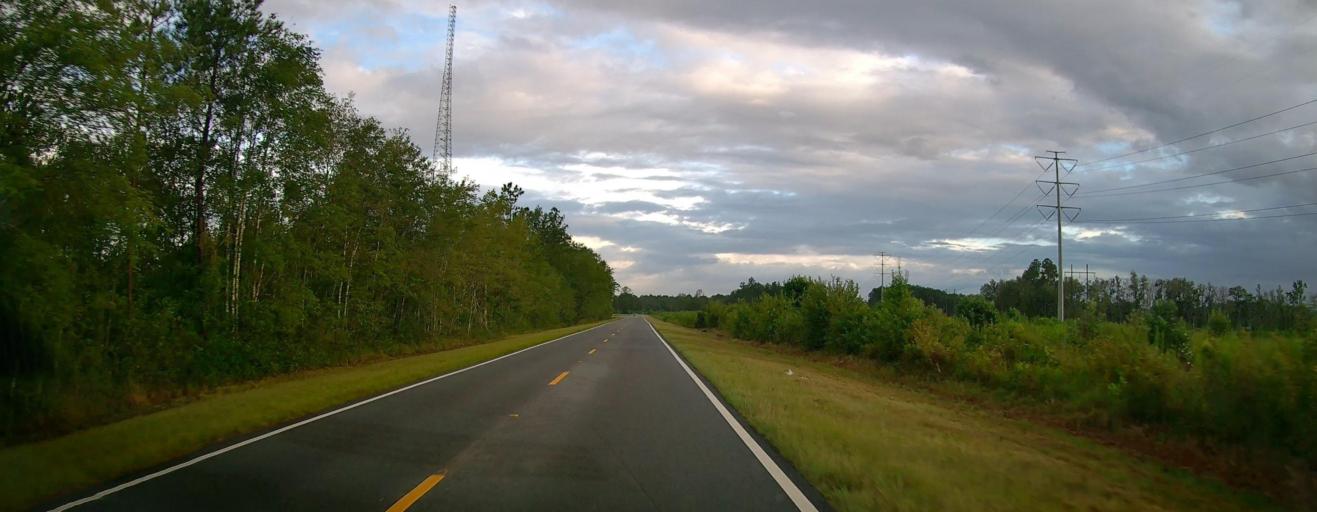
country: US
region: Georgia
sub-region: Ware County
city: Deenwood
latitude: 31.2001
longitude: -82.4015
